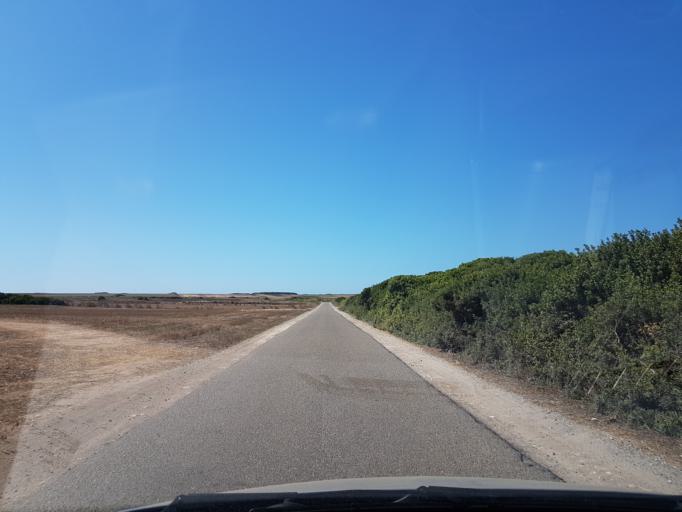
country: IT
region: Sardinia
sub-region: Provincia di Oristano
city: Nurachi
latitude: 39.9726
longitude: 8.4218
